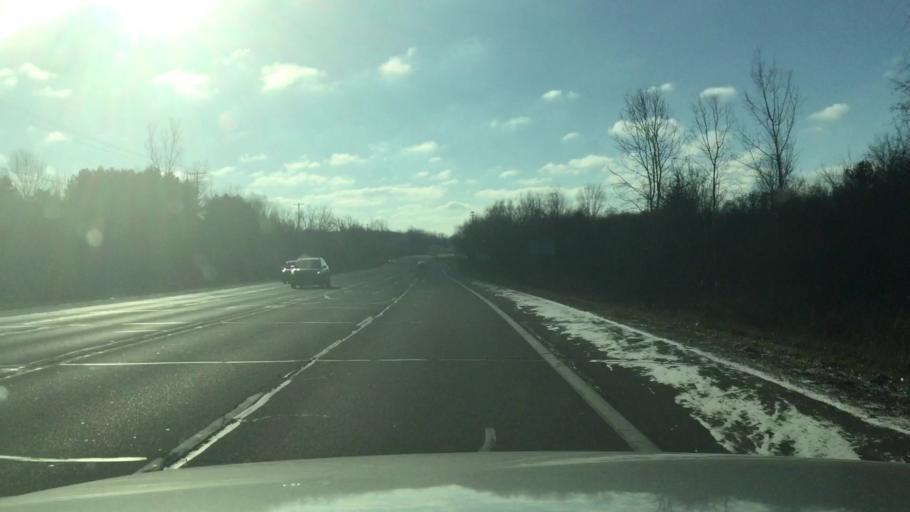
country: US
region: Michigan
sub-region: Genesee County
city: Grand Blanc
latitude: 42.9194
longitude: -83.6501
